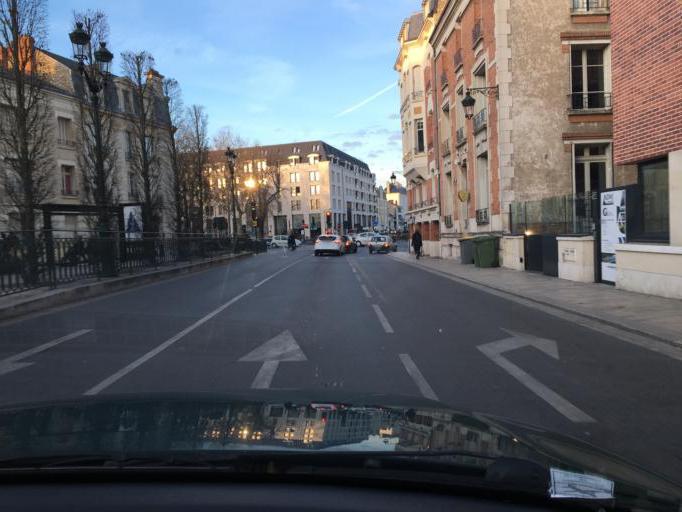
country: FR
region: Centre
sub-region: Departement du Loiret
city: Orleans
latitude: 47.9047
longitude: 1.9097
